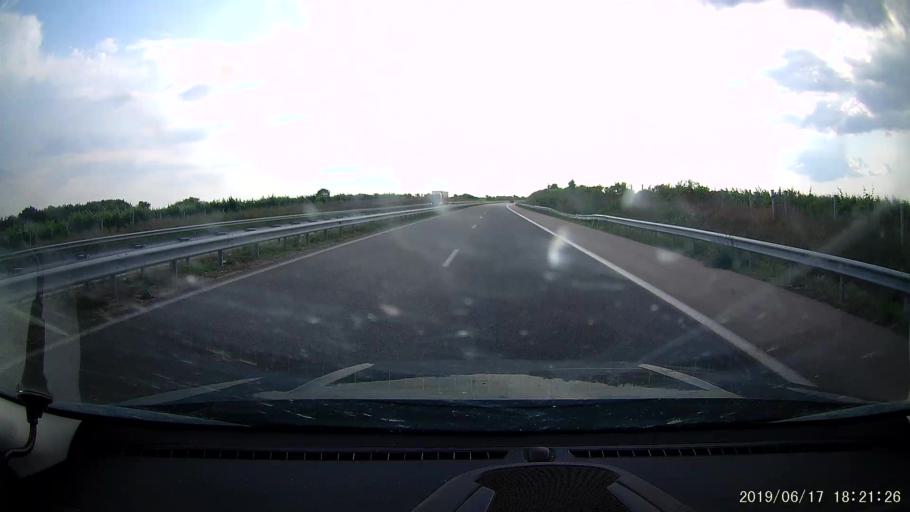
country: BG
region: Khaskovo
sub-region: Obshtina Simeonovgrad
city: Simeonovgrad
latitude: 41.9675
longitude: 25.7834
